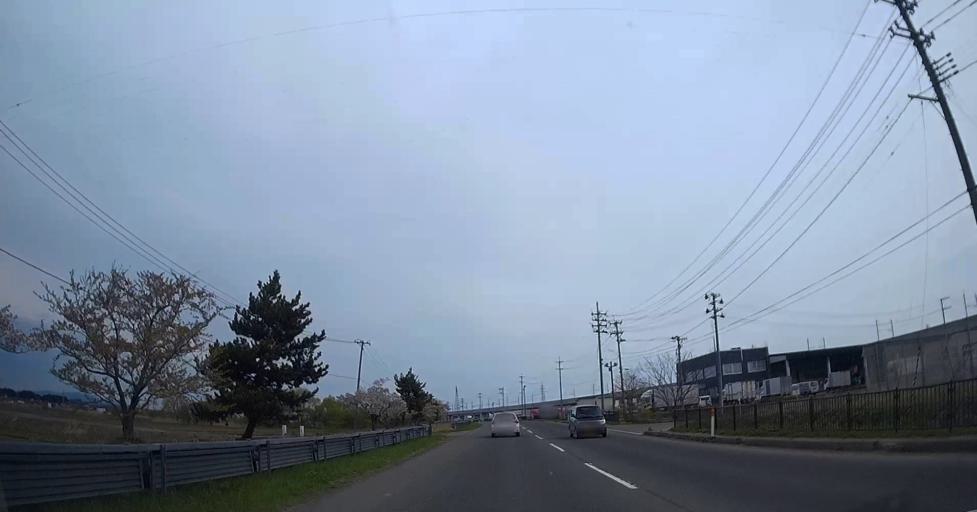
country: JP
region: Aomori
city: Aomori Shi
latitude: 40.8371
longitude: 140.6909
